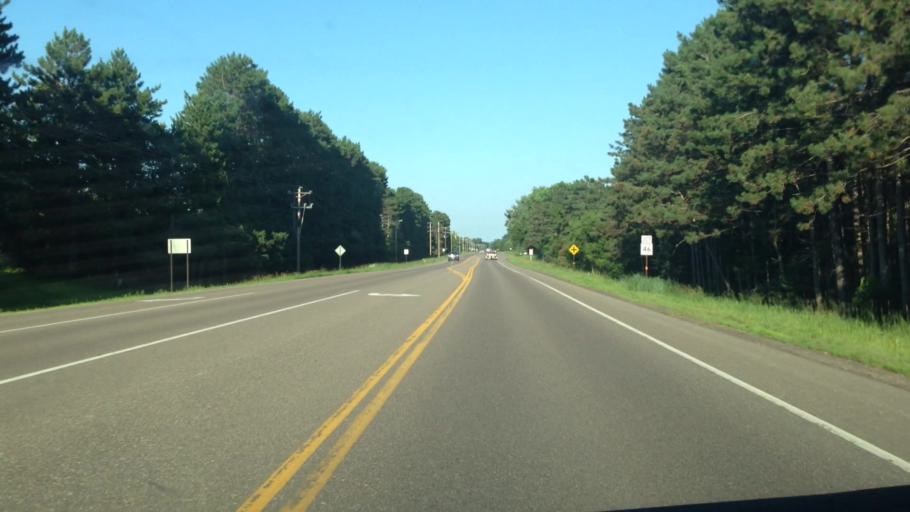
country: US
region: Minnesota
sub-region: Sherburne County
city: Zimmerman
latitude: 45.4437
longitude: -93.6190
